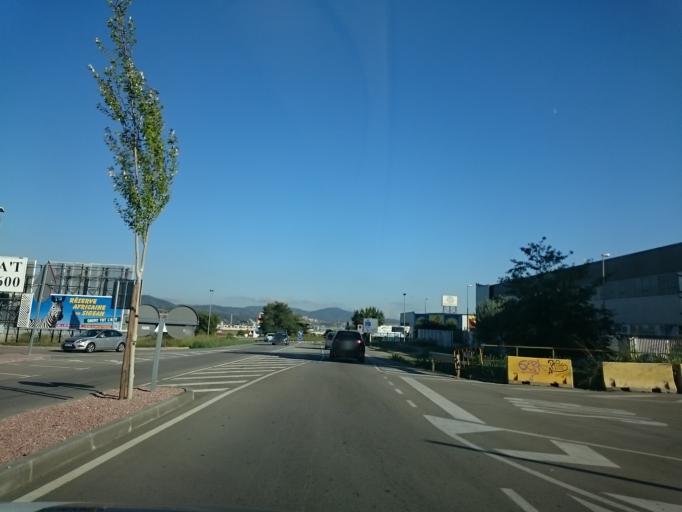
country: ES
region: Catalonia
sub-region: Provincia de Barcelona
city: Martorell
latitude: 41.4635
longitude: 1.9520
